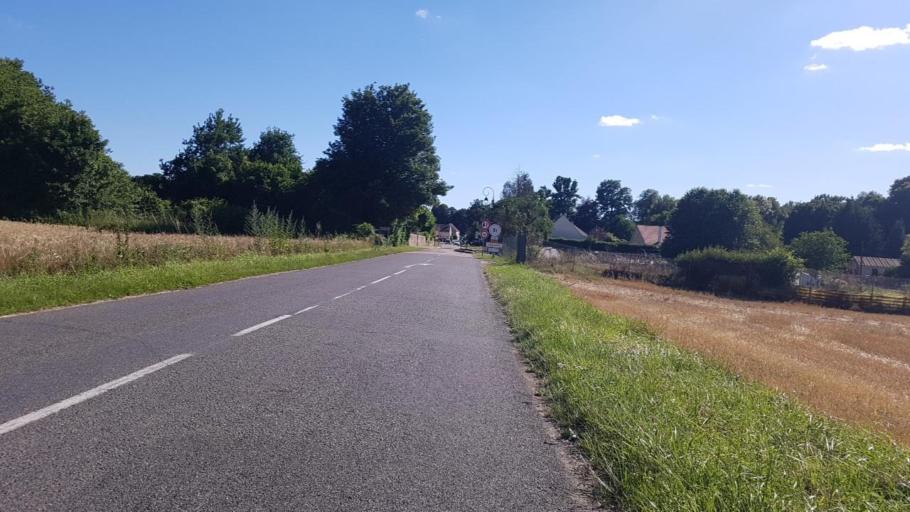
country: FR
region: Ile-de-France
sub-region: Departement de Seine-et-Marne
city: Coupvray
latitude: 48.9118
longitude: 2.7835
